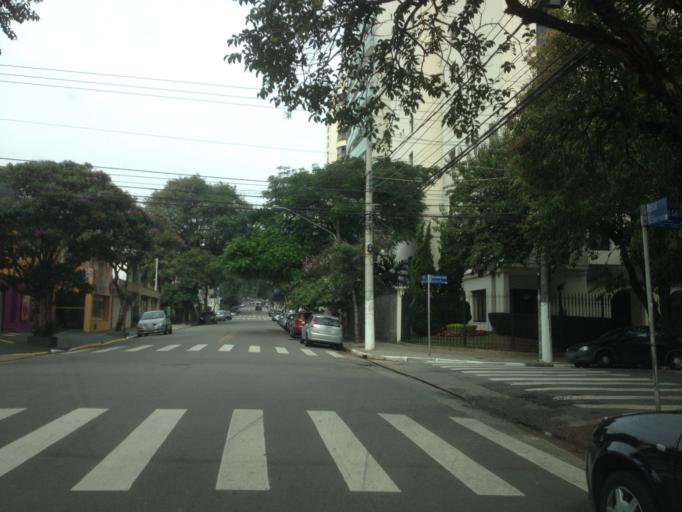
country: BR
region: Sao Paulo
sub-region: Diadema
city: Diadema
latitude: -23.6218
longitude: -46.6705
